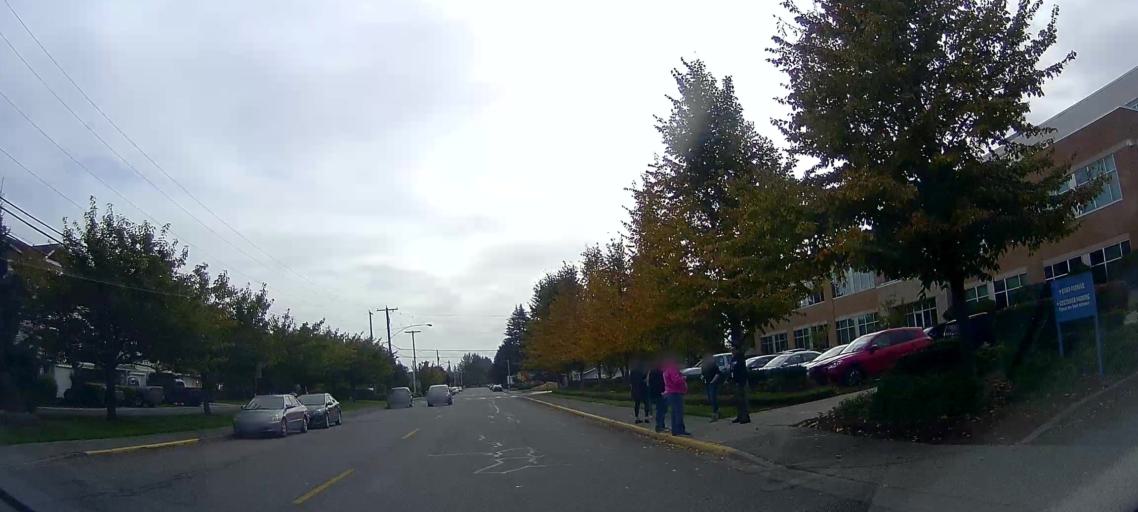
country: US
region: Washington
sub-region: Skagit County
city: Burlington
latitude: 48.4654
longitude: -122.3302
